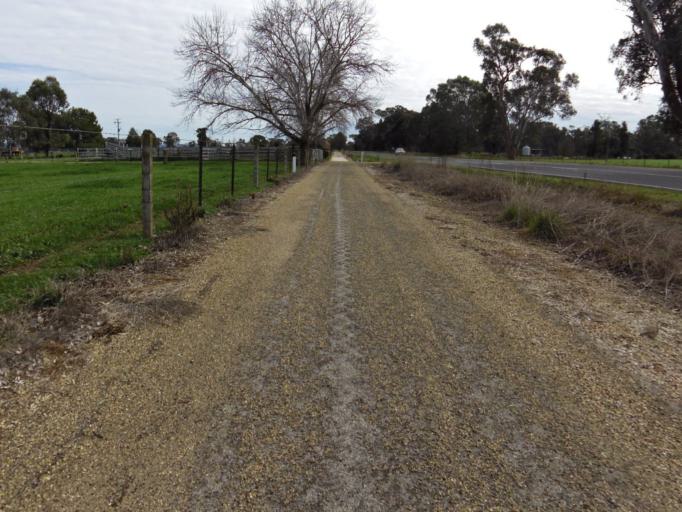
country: AU
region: Victoria
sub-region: Wangaratta
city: Wangaratta
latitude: -36.4114
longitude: 146.3526
